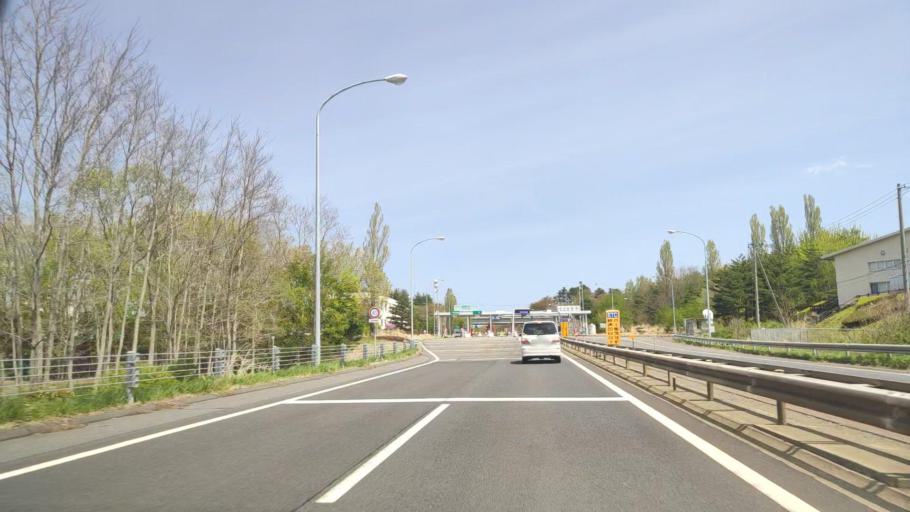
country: JP
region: Aomori
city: Hachinohe
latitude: 40.4850
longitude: 141.4617
